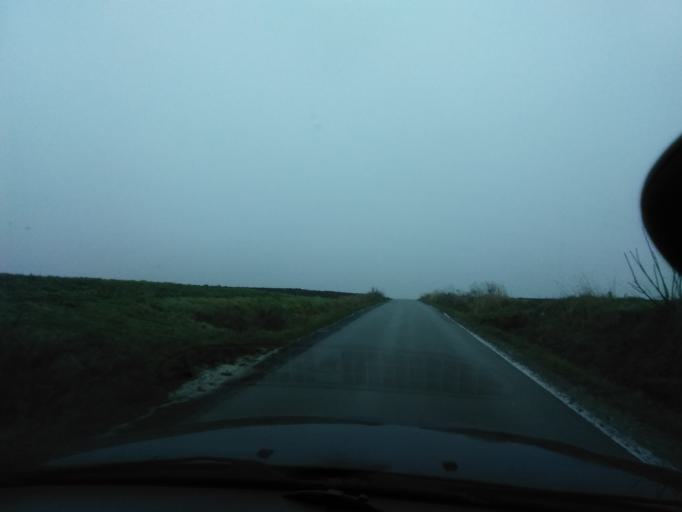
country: PL
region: Subcarpathian Voivodeship
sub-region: Powiat lancucki
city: Markowa
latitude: 50.0299
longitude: 22.3185
